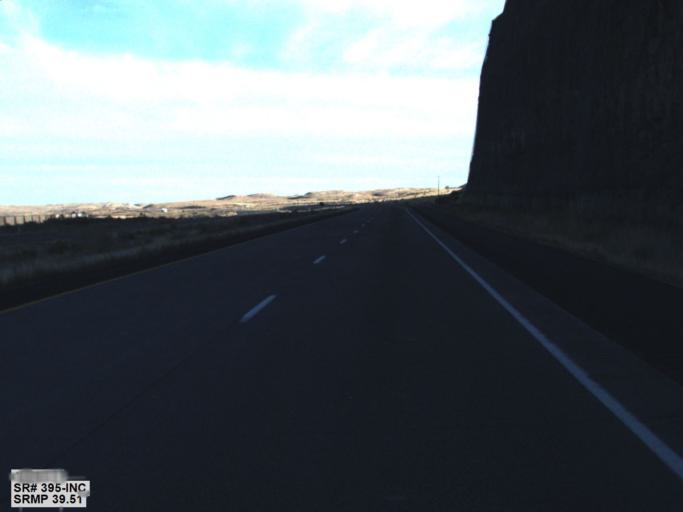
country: US
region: Washington
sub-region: Franklin County
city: Basin City
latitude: 46.4788
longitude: -119.0106
